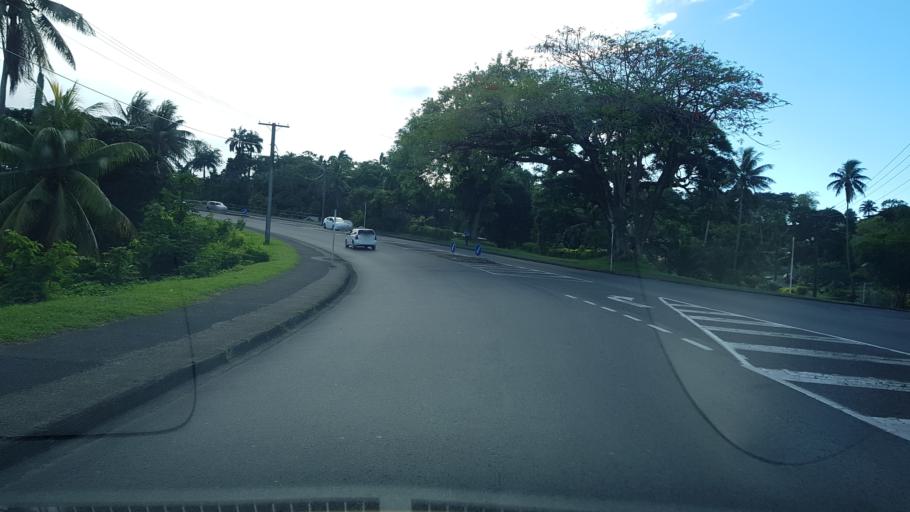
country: FJ
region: Central
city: Suva
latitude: -18.1457
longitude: 178.4381
